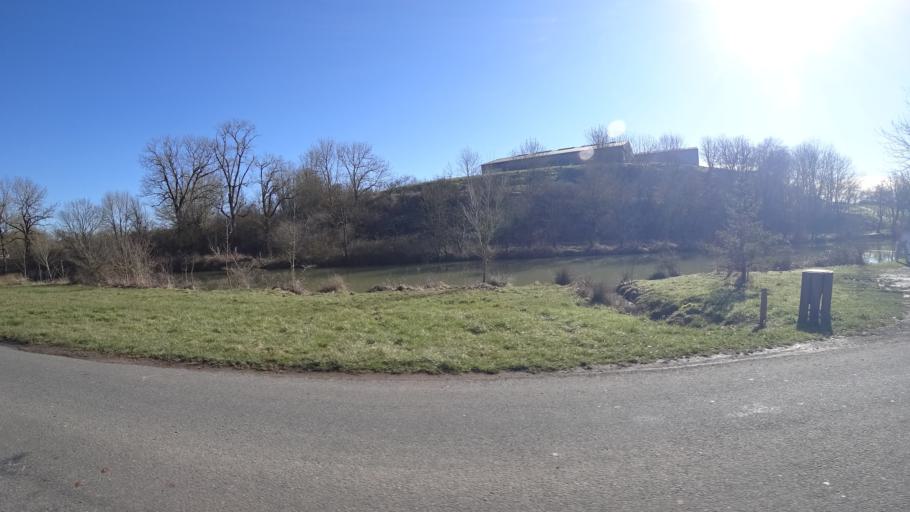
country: FR
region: Midi-Pyrenees
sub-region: Departement de l'Aveyron
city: Rodez
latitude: 44.3825
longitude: 2.5813
